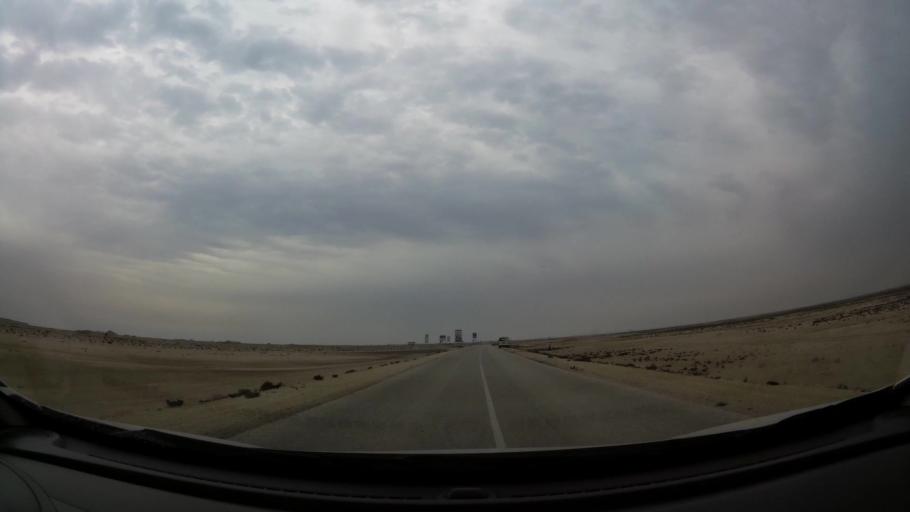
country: BH
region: Central Governorate
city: Dar Kulayb
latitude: 25.8730
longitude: 50.5980
